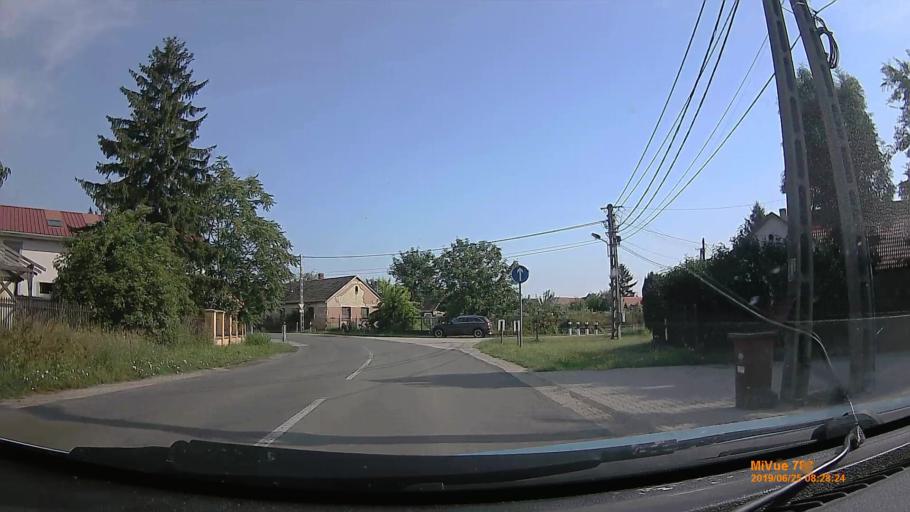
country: HU
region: Fejer
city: Szabadbattyan
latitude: 47.1184
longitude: 18.3752
